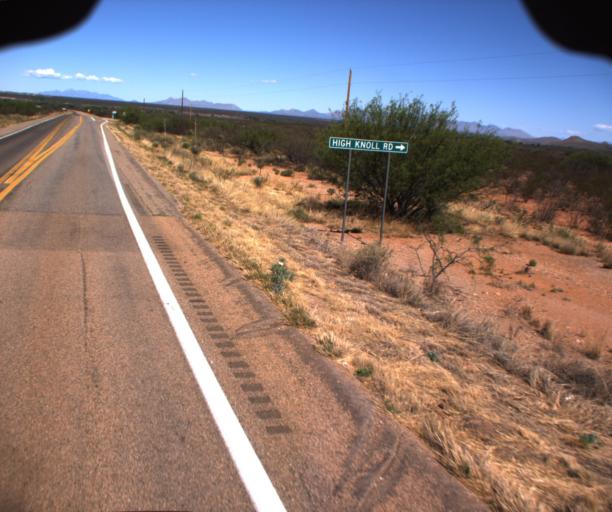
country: US
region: Arizona
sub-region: Cochise County
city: Sierra Vista Southeast
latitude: 31.5509
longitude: -110.1141
